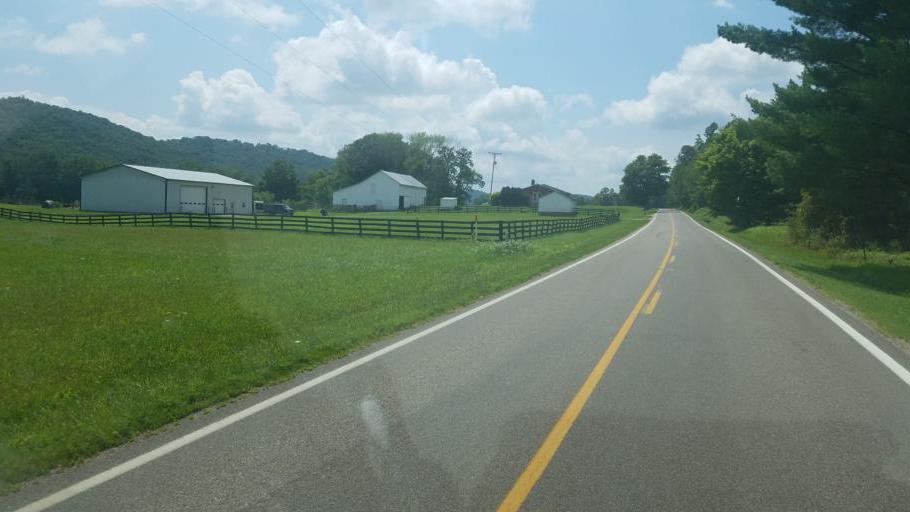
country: US
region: Ohio
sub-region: Ross County
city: Kingston
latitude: 39.3294
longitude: -82.7306
